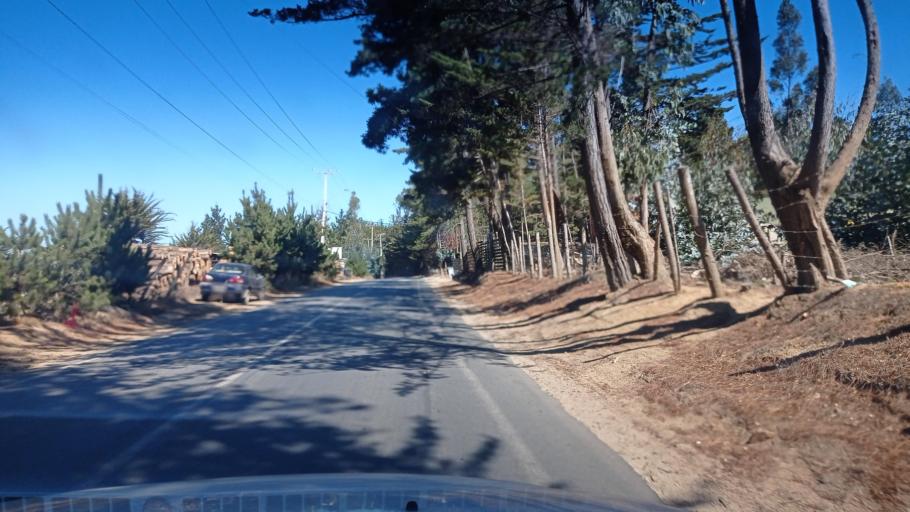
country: CL
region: O'Higgins
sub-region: Provincia de Colchagua
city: Santa Cruz
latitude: -34.4153
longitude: -71.9991
